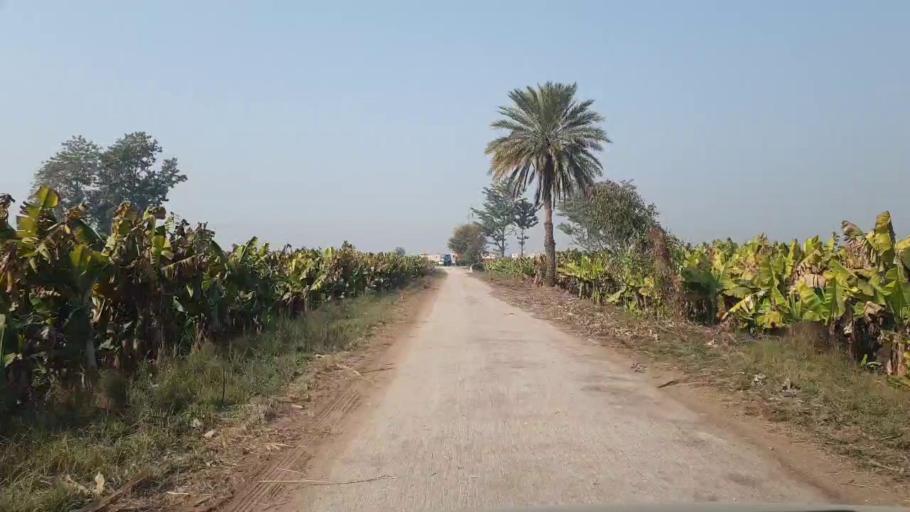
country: PK
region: Sindh
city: Sakrand
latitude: 25.9917
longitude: 68.3635
